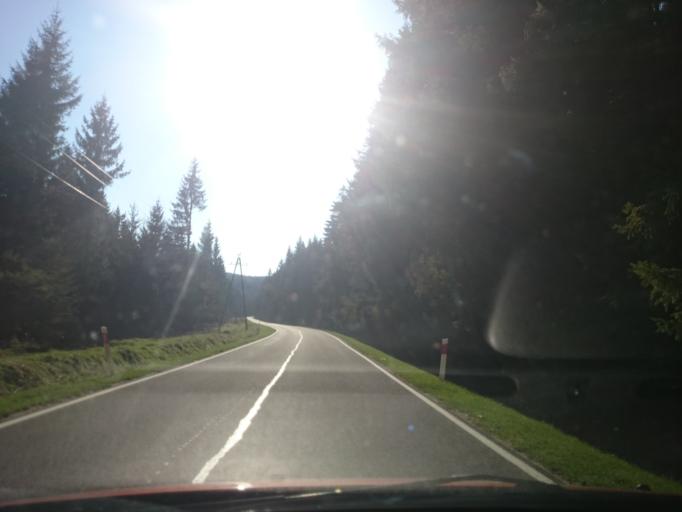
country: PL
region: Lower Silesian Voivodeship
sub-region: Powiat klodzki
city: Duszniki-Zdroj
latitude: 50.3253
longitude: 16.4260
